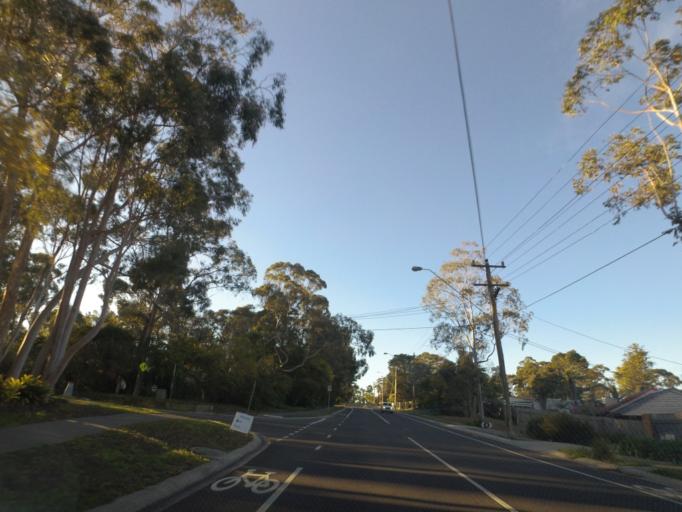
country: AU
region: Victoria
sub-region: Manningham
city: Park Orchards
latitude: -37.7806
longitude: 145.2107
